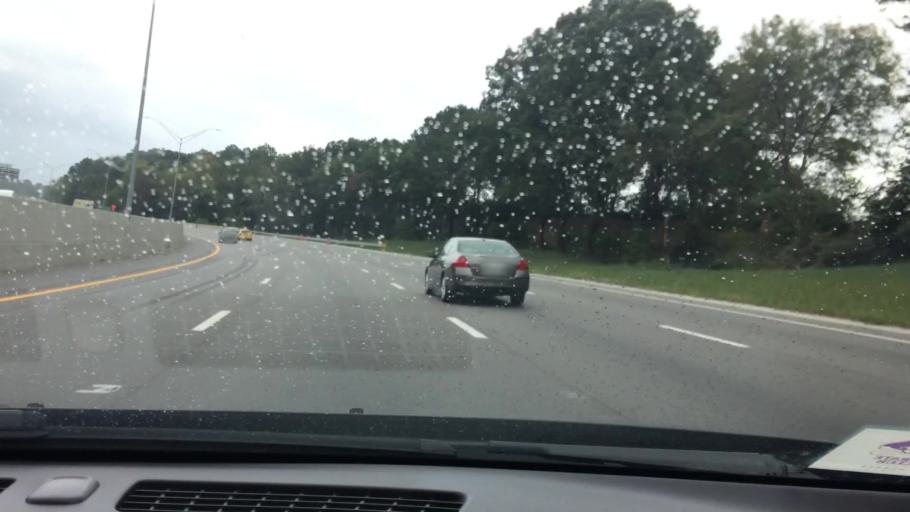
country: US
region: North Carolina
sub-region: Wake County
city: Raleigh
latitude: 35.7529
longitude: -78.6238
